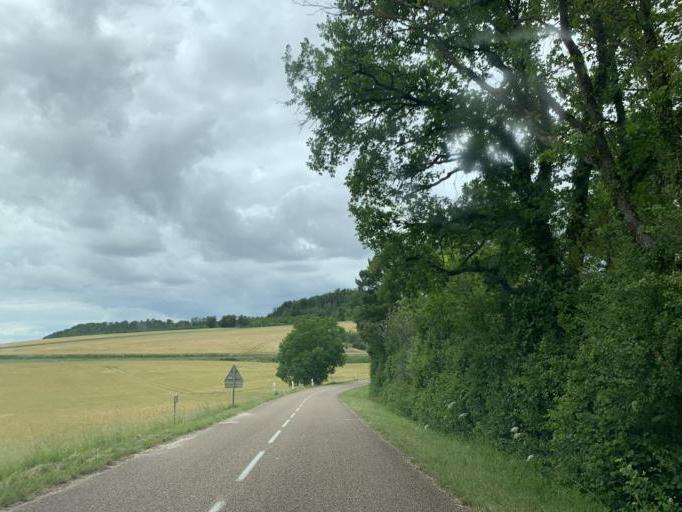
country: FR
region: Bourgogne
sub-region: Departement de l'Yonne
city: Saint-Bris-le-Vineux
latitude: 47.7250
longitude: 3.6942
